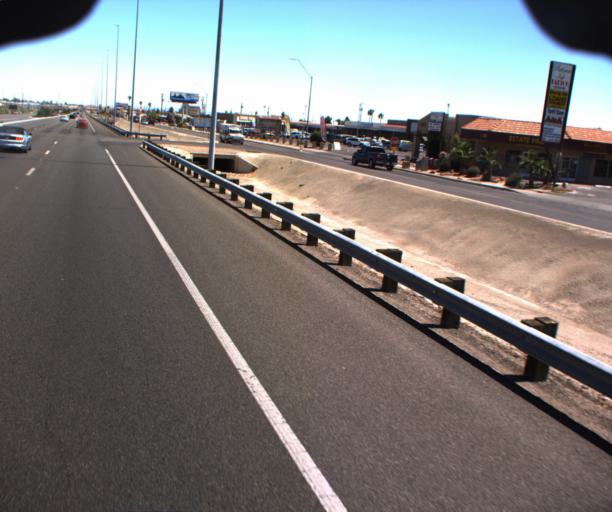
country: US
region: Arizona
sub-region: Maricopa County
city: El Mirage
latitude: 33.6200
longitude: -112.3265
